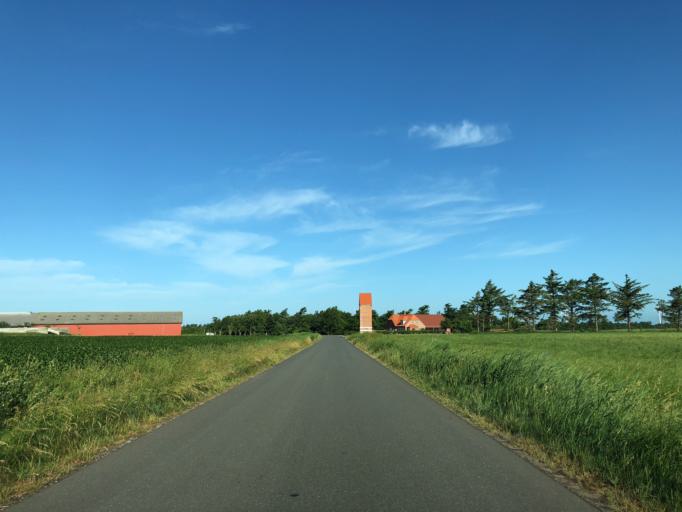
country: DK
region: Central Jutland
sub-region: Holstebro Kommune
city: Ulfborg
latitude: 56.3380
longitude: 8.2937
